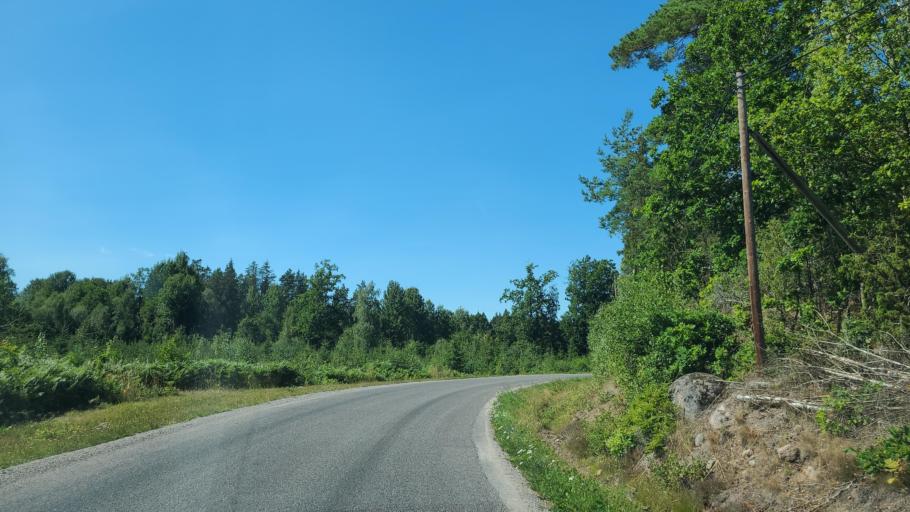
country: SE
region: Kalmar
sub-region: Kalmar Kommun
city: Ljungbyholm
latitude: 56.5707
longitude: 16.0709
